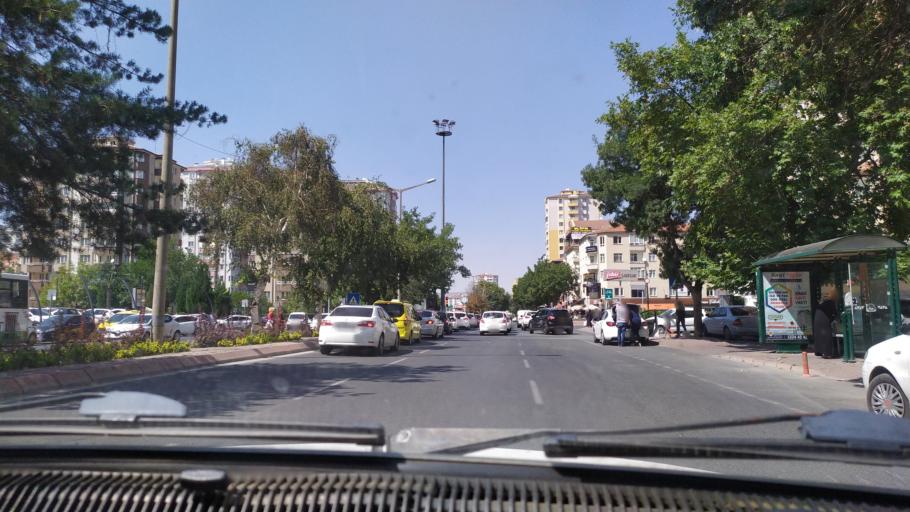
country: TR
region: Kayseri
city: Kayseri
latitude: 38.7272
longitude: 35.5193
